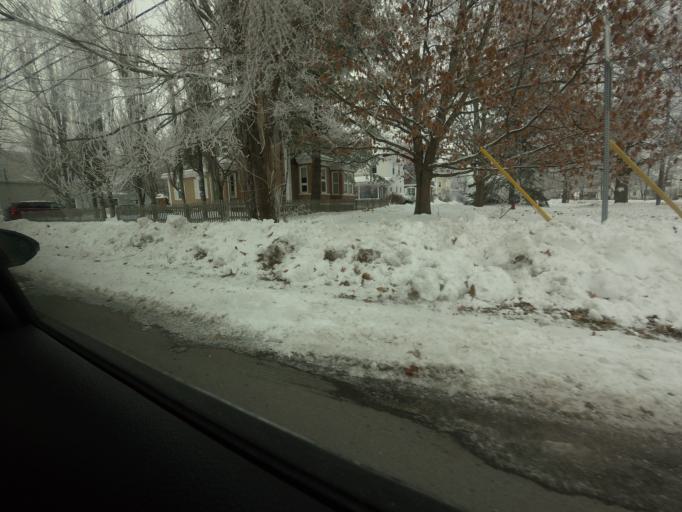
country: CA
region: New Brunswick
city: Fredericton
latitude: 45.9546
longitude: -66.6352
